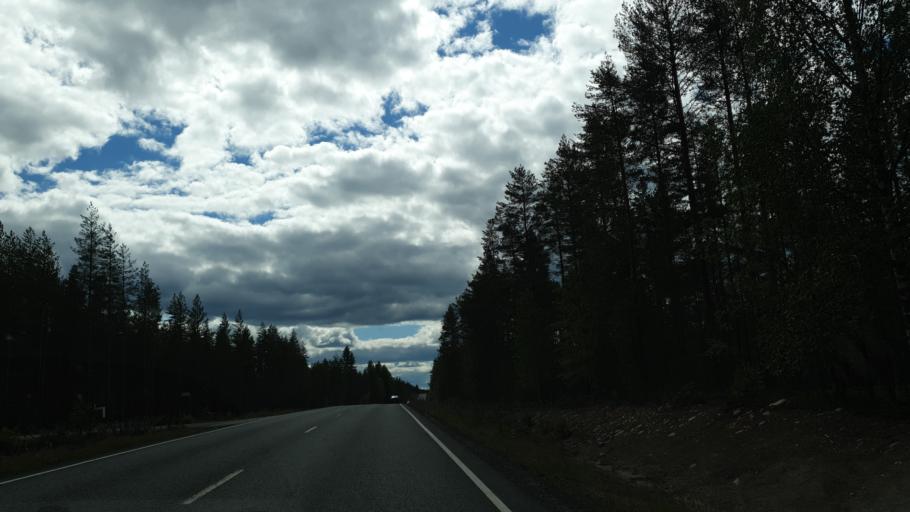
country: FI
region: Kainuu
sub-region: Kehys-Kainuu
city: Kuhmo
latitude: 64.0917
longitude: 29.4803
